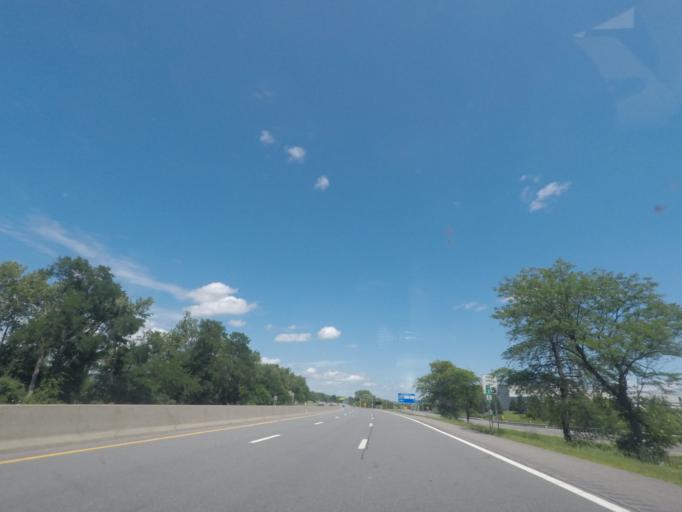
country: US
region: New York
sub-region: Schenectady County
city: Scotia
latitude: 42.8129
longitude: -73.9677
